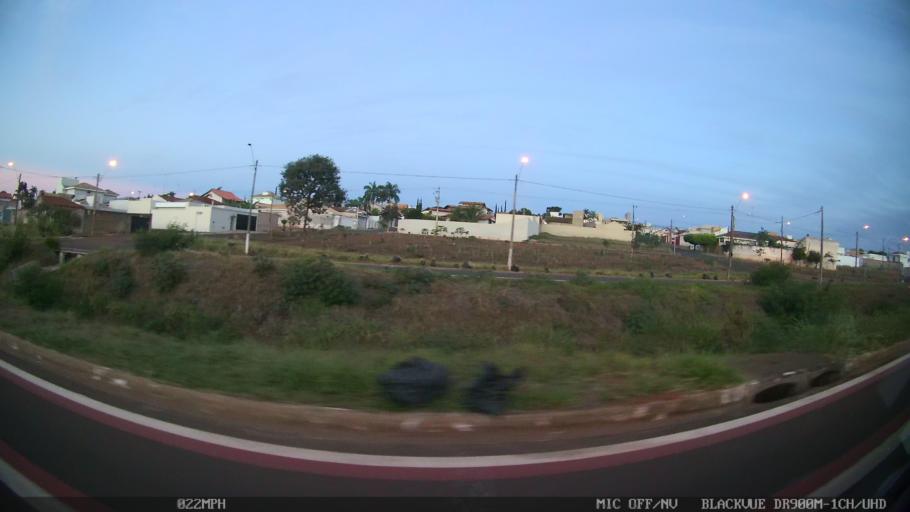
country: BR
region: Sao Paulo
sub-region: Catanduva
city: Catanduva
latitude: -21.1463
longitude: -48.9918
